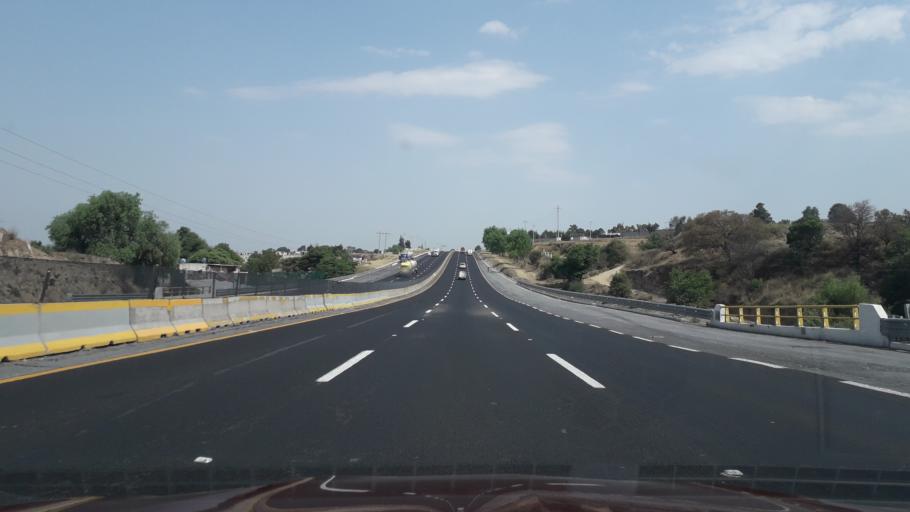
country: MX
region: Puebla
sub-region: San Salvador el Verde
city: San Lucas el Grande
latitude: 19.2979
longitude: -98.4785
